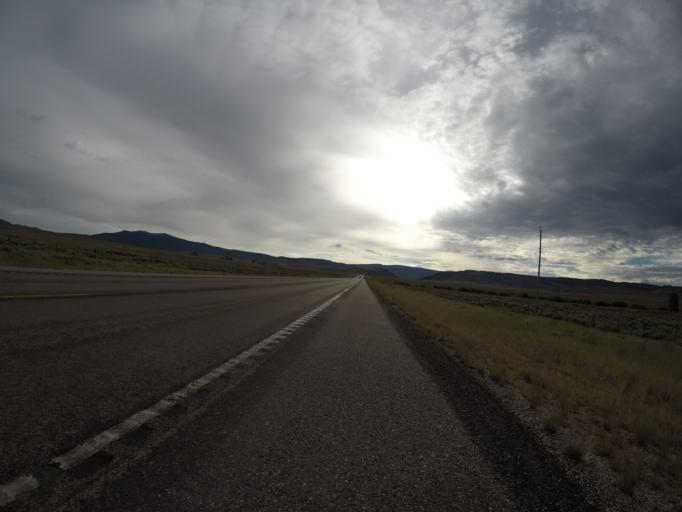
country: US
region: Wyoming
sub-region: Carbon County
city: Saratoga
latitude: 41.3546
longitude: -106.6078
